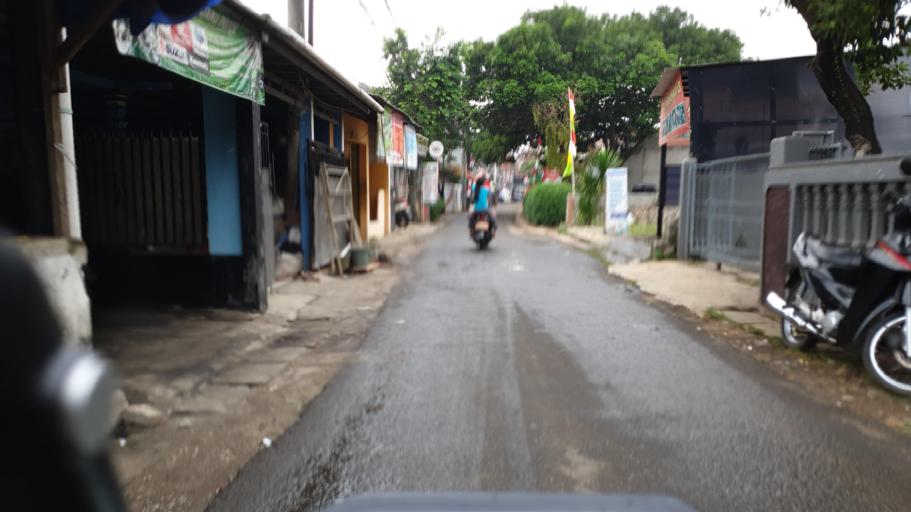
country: ID
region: West Java
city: Pamulang
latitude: -6.3339
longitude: 106.7697
